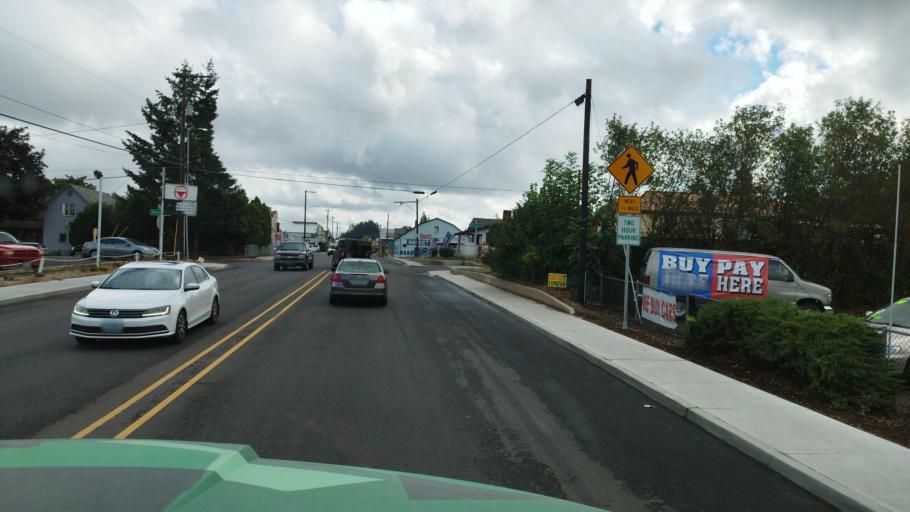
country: US
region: Oregon
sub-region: Yamhill County
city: Lafayette
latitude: 45.2449
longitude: -123.1184
